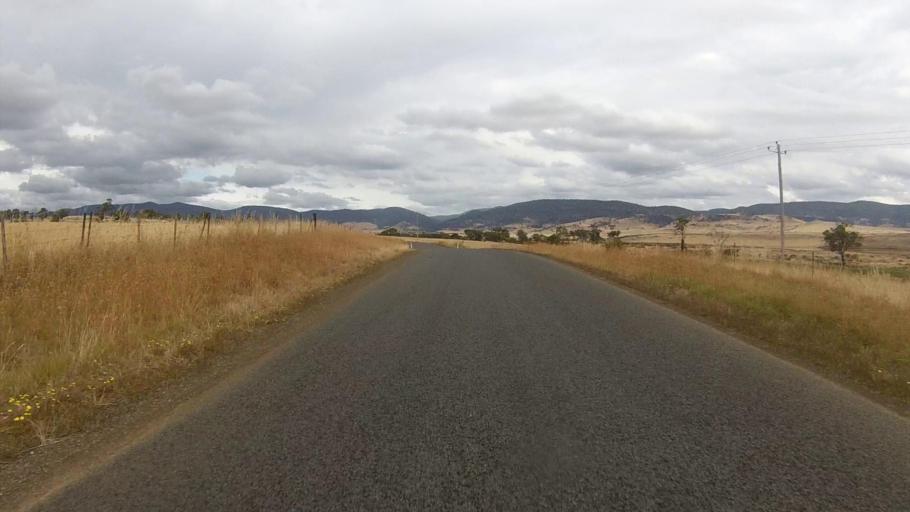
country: AU
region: Tasmania
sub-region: Northern Midlands
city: Evandale
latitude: -41.8041
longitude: 147.7526
